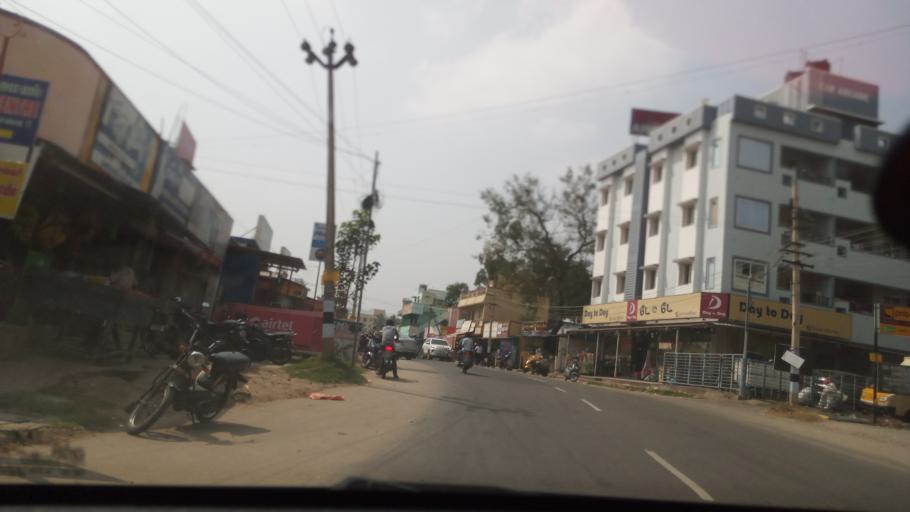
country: IN
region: Tamil Nadu
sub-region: Coimbatore
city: Perur
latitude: 11.0250
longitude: 76.9026
